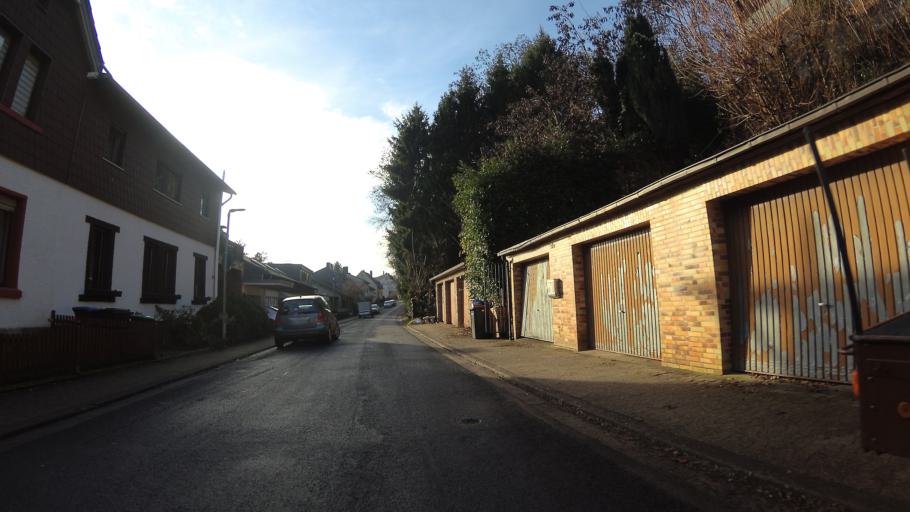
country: DE
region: Saarland
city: Spiesen-Elversberg
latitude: 49.3104
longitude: 7.1297
